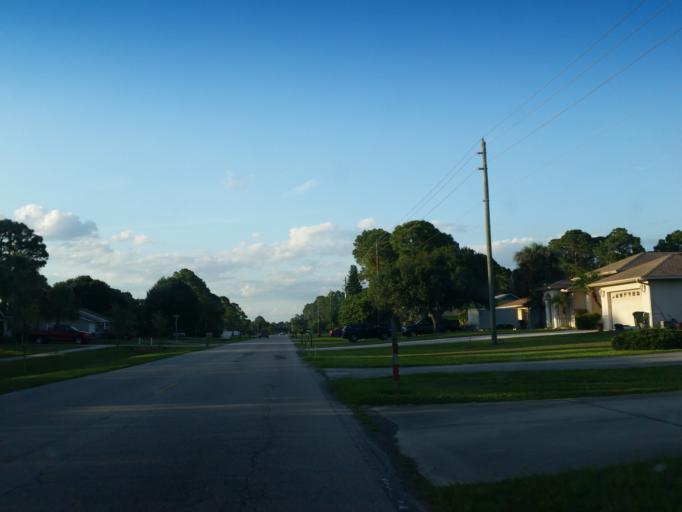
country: US
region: Florida
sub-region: Sarasota County
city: North Port
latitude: 27.0622
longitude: -82.1981
